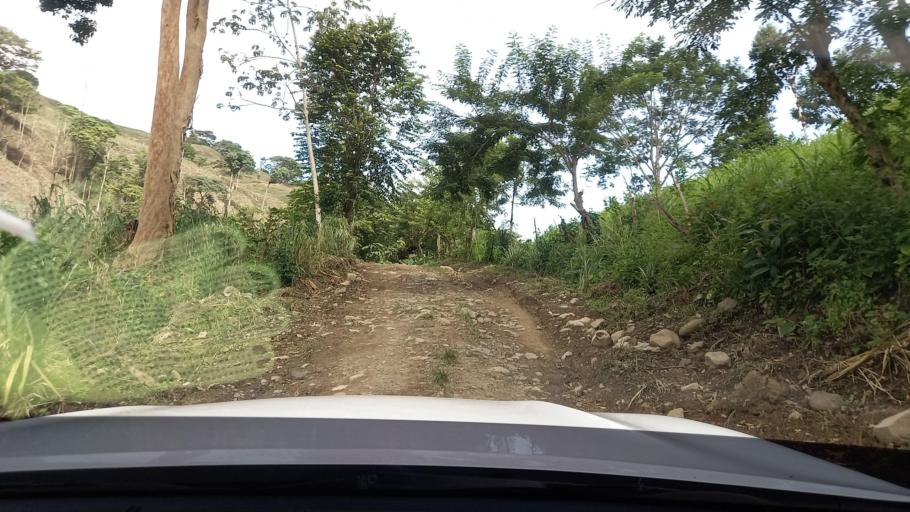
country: NI
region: Jinotega
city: San Jose de Bocay
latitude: 13.4005
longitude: -85.6993
